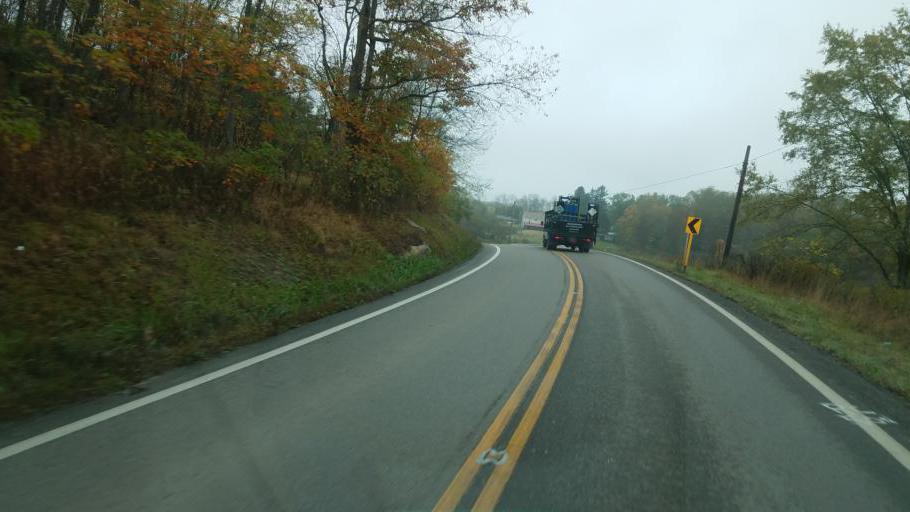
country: US
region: Ohio
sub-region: Carroll County
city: Carrollton
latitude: 40.4168
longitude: -81.1392
